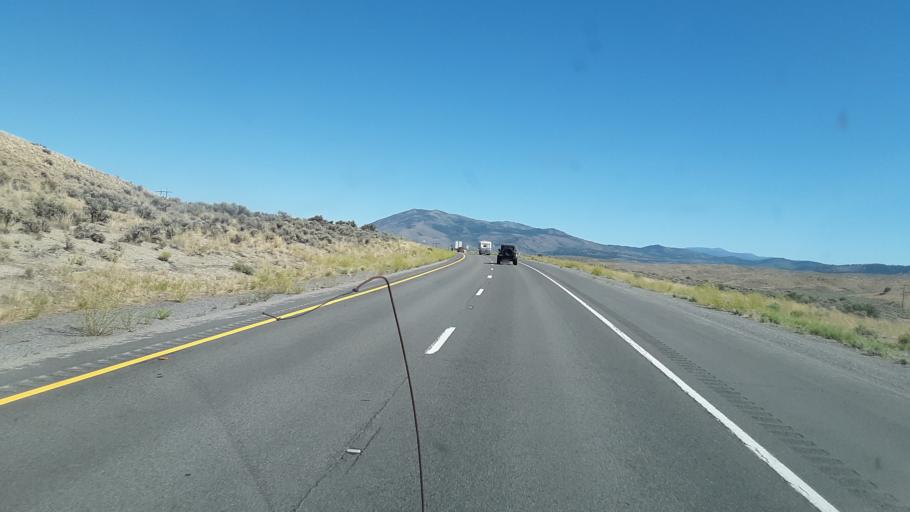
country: US
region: Nevada
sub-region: Washoe County
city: Cold Springs
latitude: 39.7019
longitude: -120.0327
